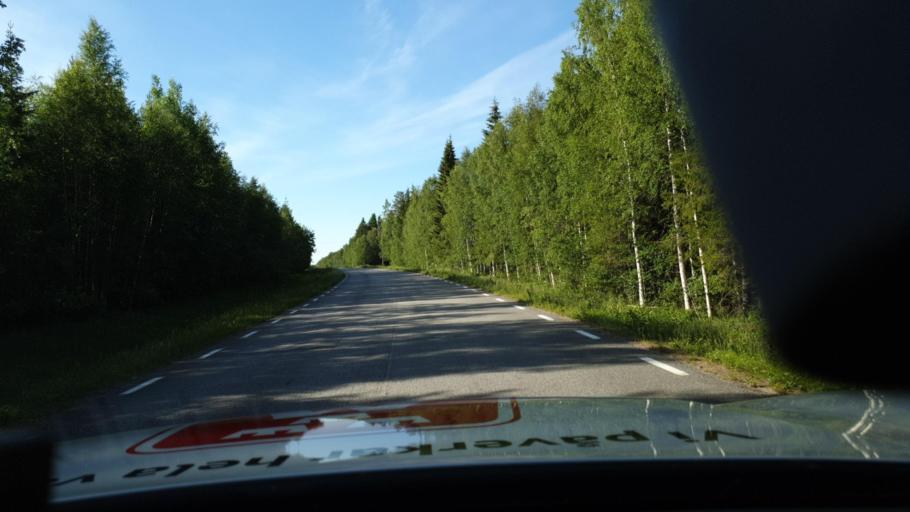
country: SE
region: Norrbotten
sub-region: Kalix Kommun
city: Toere
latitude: 65.8697
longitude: 22.6765
